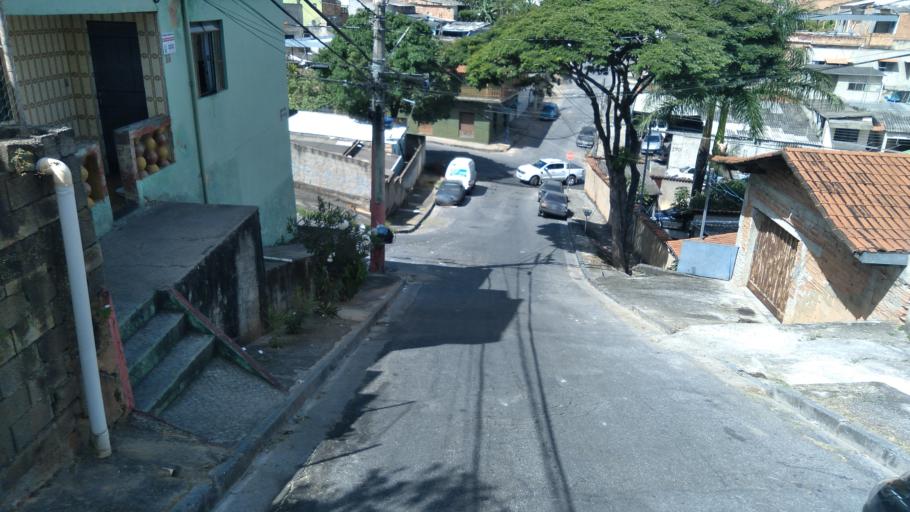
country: BR
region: Minas Gerais
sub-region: Belo Horizonte
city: Belo Horizonte
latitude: -19.8640
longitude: -43.9071
